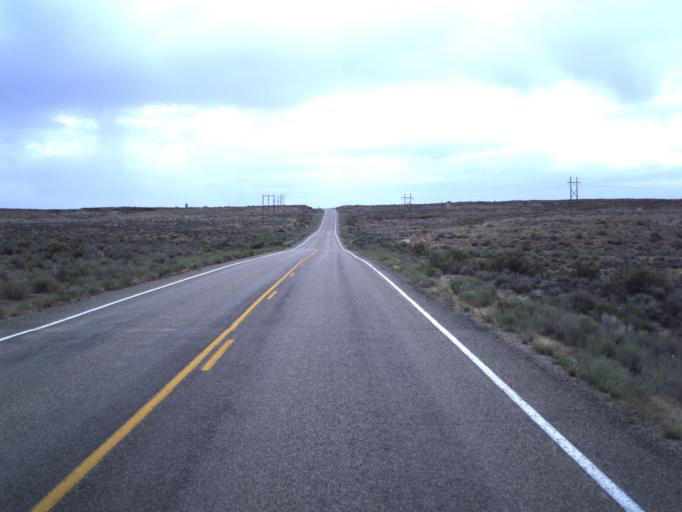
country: US
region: Colorado
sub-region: Rio Blanco County
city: Rangely
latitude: 40.0707
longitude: -109.2034
